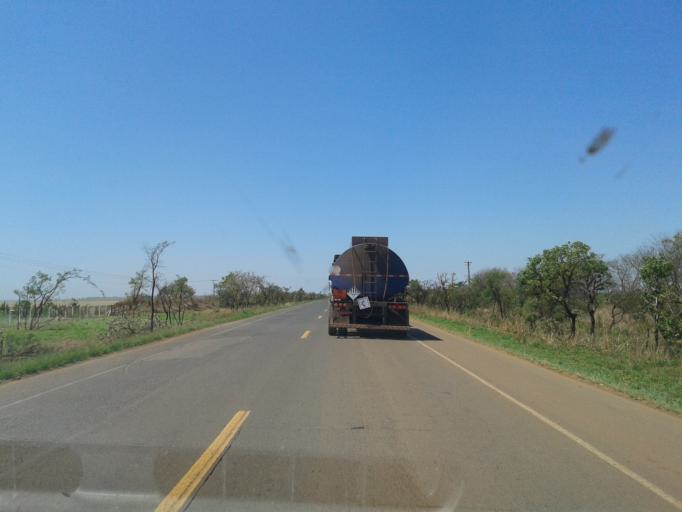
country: BR
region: Minas Gerais
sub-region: Araxa
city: Araxa
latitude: -19.3157
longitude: -47.3877
